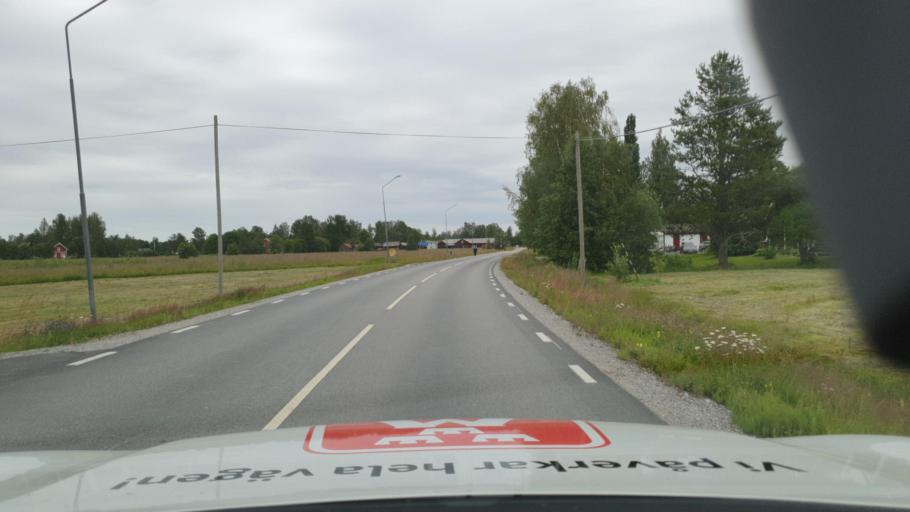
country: SE
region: Vaesterbotten
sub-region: Nordmalings Kommun
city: Nordmaling
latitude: 63.5479
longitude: 19.3774
